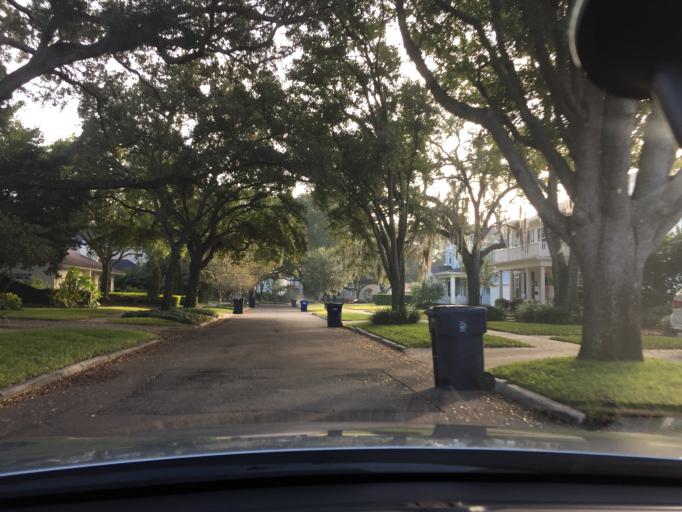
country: US
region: Florida
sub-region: Hillsborough County
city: Tampa
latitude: 27.9359
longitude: -82.4913
